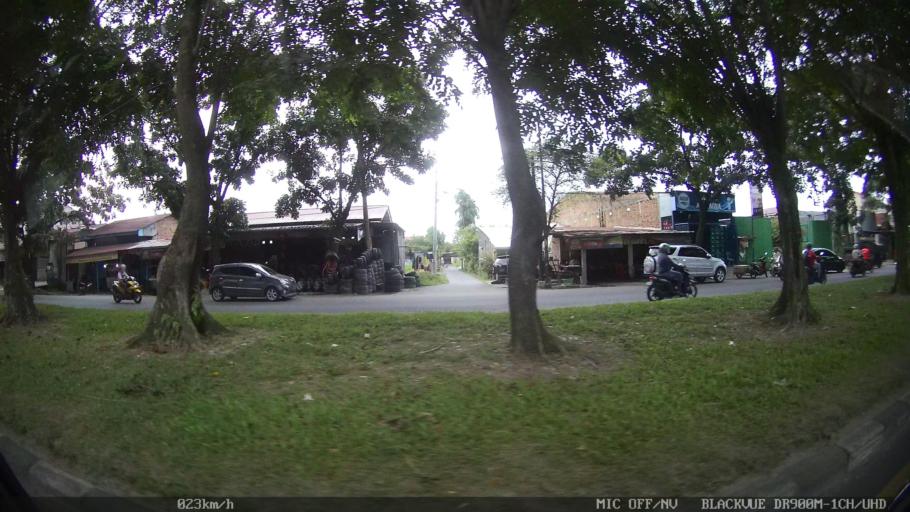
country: ID
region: North Sumatra
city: Sunggal
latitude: 3.5406
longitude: 98.6461
